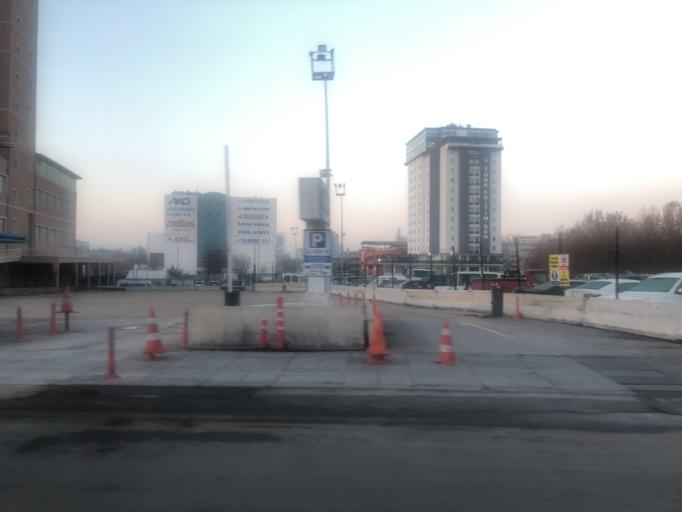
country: TR
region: Ankara
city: Ankara
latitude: 39.9522
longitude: 32.8569
